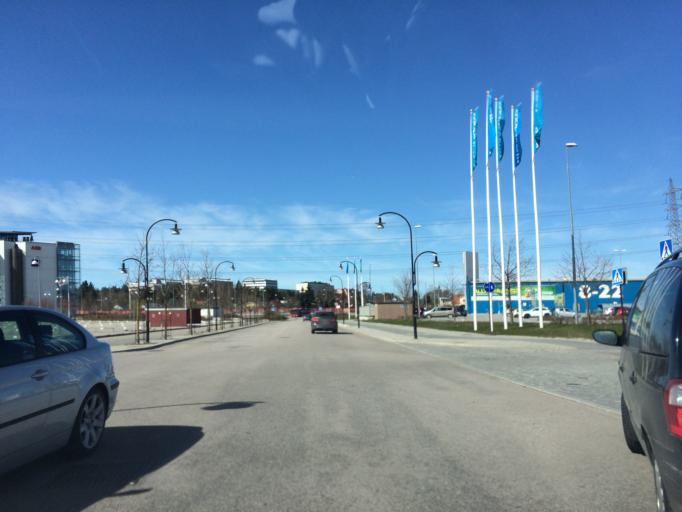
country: SE
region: Stockholm
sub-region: Sollentuna Kommun
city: Sollentuna
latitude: 59.4394
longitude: 17.9339
